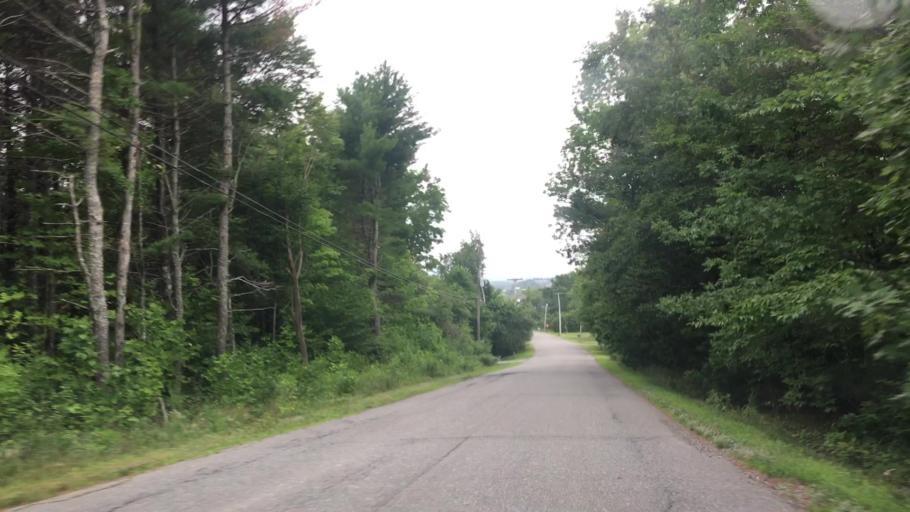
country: US
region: Maine
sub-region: Penobscot County
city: Veazie
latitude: 44.8459
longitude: -68.7466
